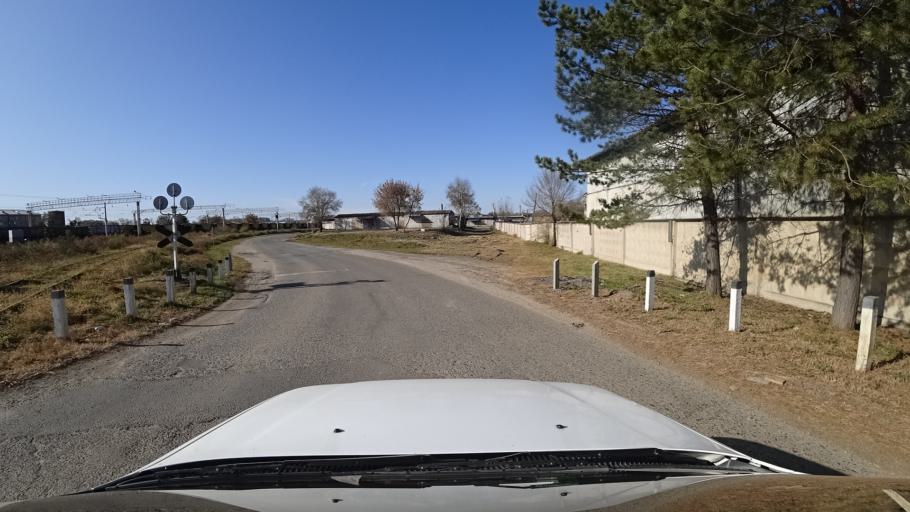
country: RU
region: Primorskiy
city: Dal'nerechensk
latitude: 45.9384
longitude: 133.7290
